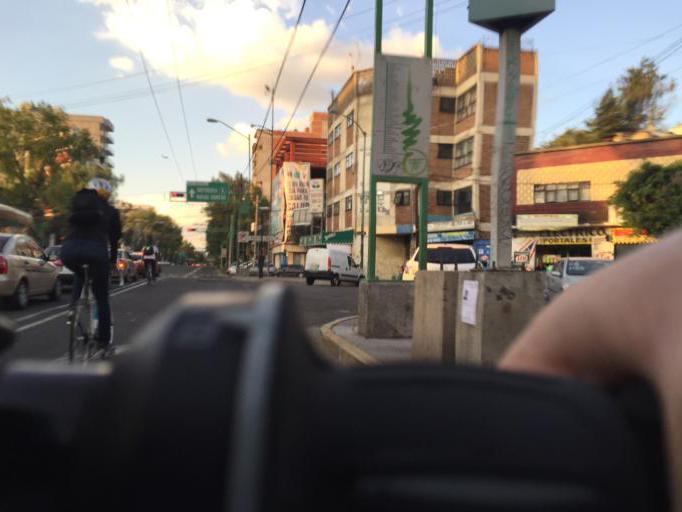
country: MX
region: Mexico City
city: Colonia Nativitas
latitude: 19.3688
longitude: -99.1501
